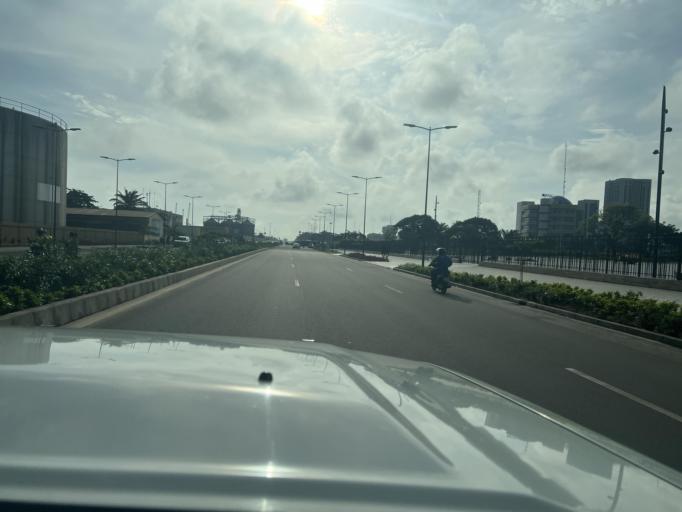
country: BJ
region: Littoral
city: Cotonou
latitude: 6.3514
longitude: 2.4305
